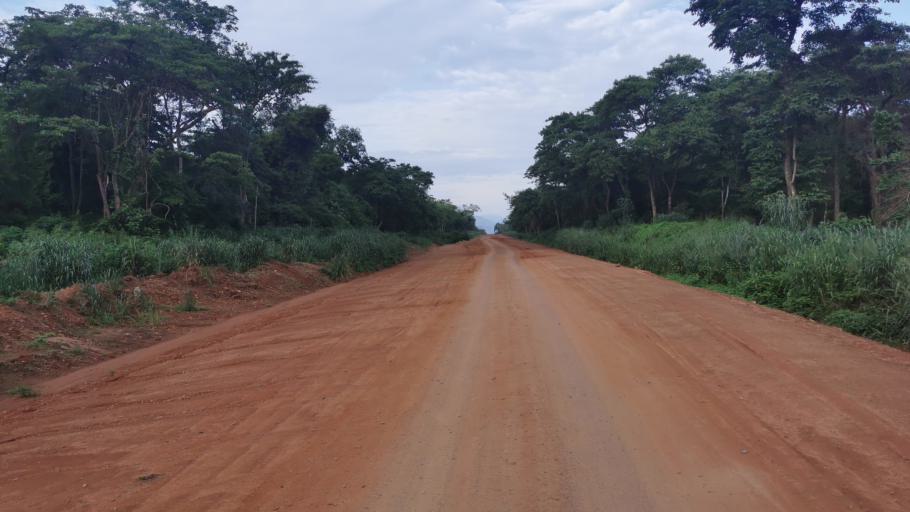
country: ET
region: Gambela
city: Gambela
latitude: 7.5874
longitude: 34.7462
